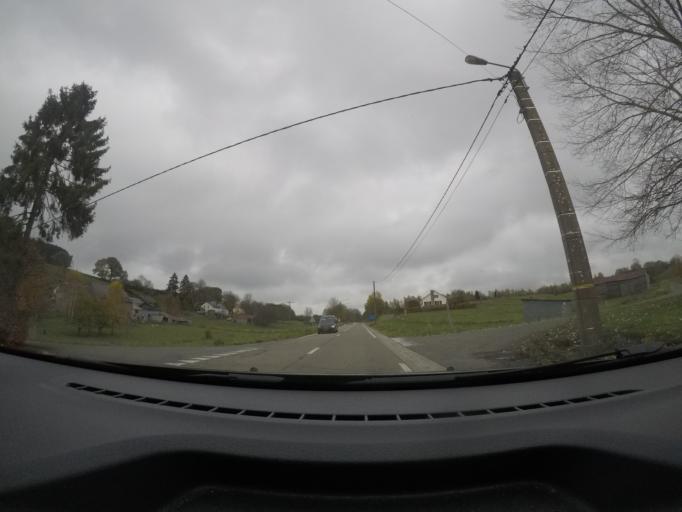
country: BE
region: Wallonia
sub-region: Province du Luxembourg
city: Houffalize
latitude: 50.0980
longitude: 5.7456
